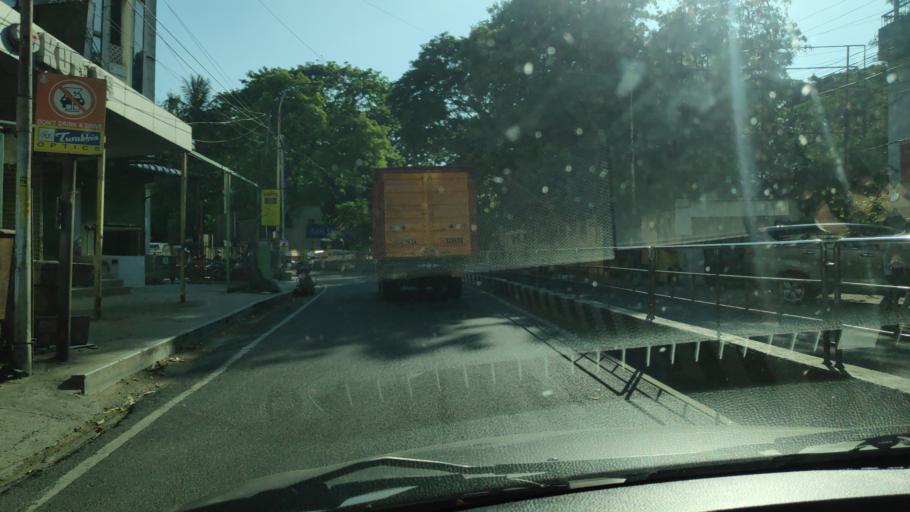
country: IN
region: Tamil Nadu
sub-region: Chennai
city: Chetput
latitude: 13.0645
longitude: 80.2366
